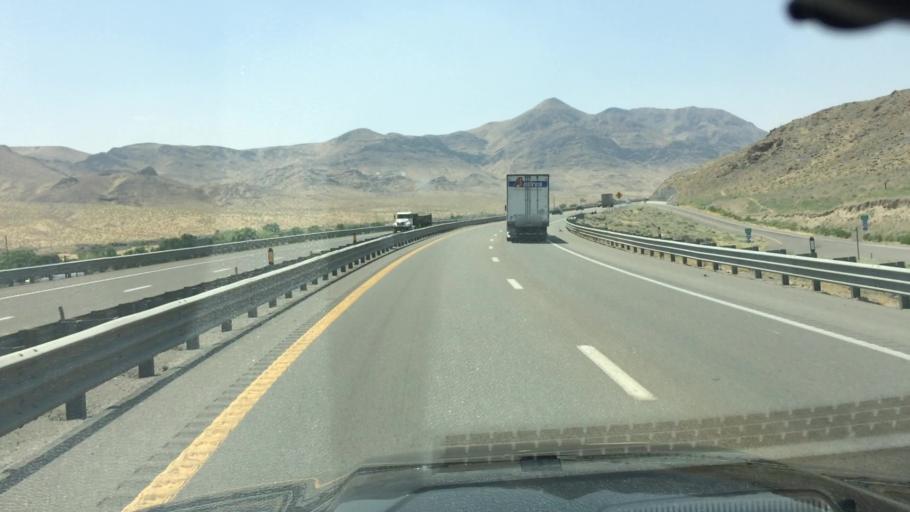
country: US
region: Nevada
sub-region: Lyon County
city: Fernley
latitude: 39.5919
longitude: -119.3688
